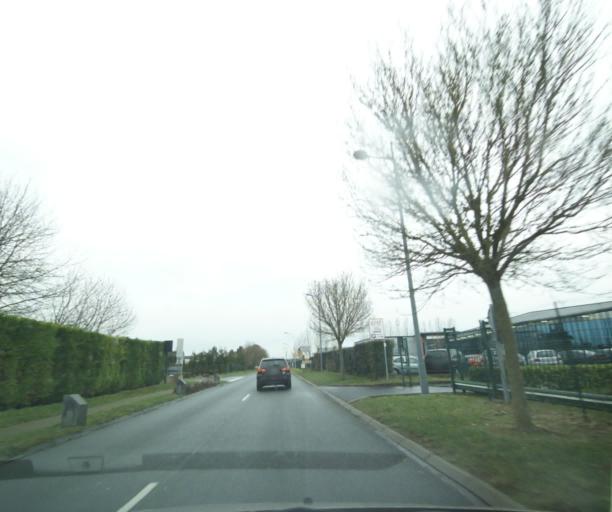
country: FR
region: Nord-Pas-de-Calais
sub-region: Departement du Nord
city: Prouvy
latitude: 50.3268
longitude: 3.4476
